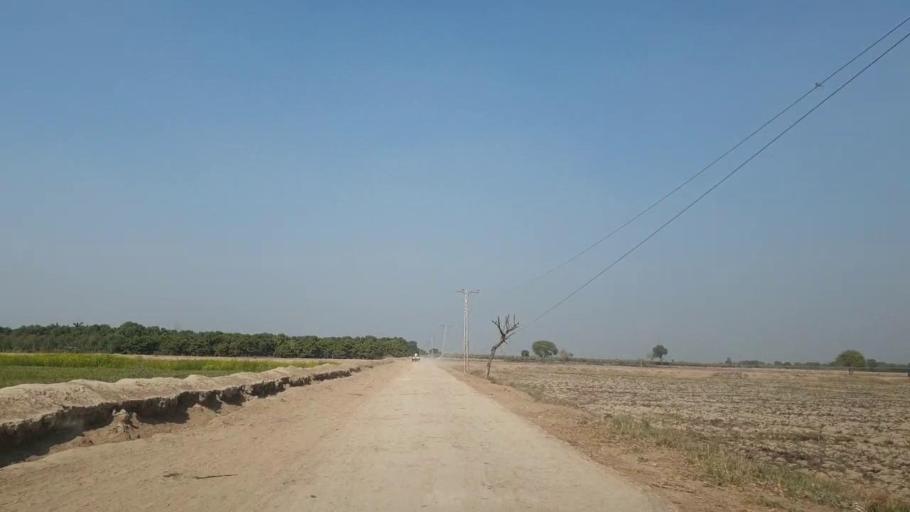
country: PK
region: Sindh
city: Tando Allahyar
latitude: 25.4991
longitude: 68.8221
